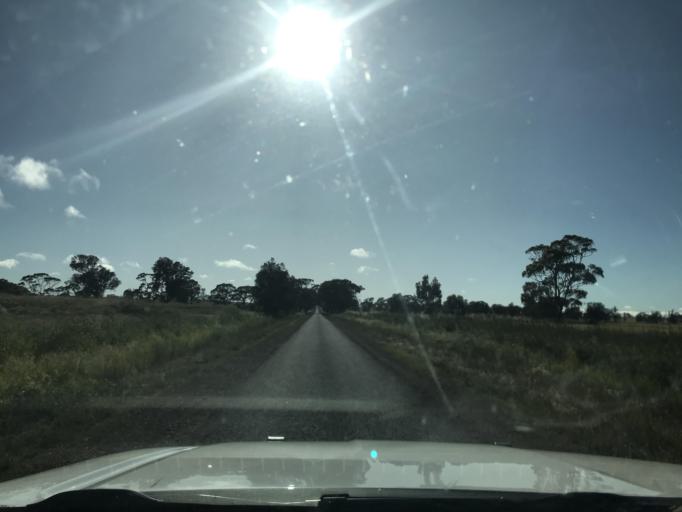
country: AU
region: Victoria
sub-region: Horsham
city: Horsham
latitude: -36.6966
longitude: 141.5899
